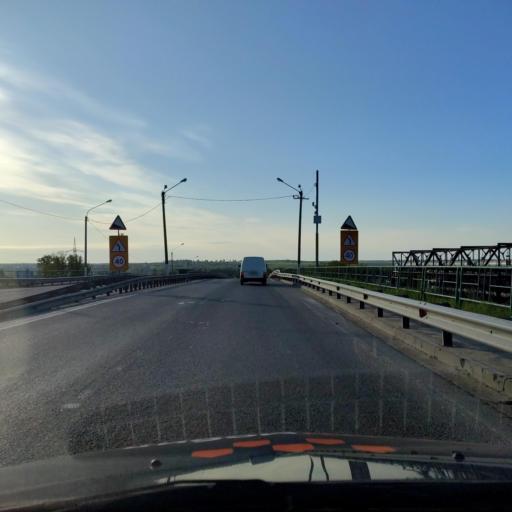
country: RU
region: Lipetsk
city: Yelets
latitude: 52.5918
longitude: 38.4918
